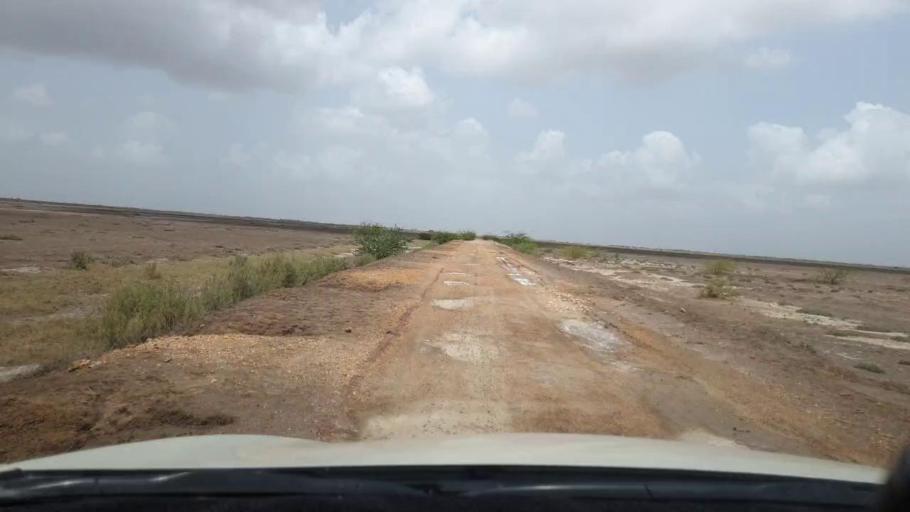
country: PK
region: Sindh
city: Kadhan
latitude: 24.3603
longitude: 68.8377
